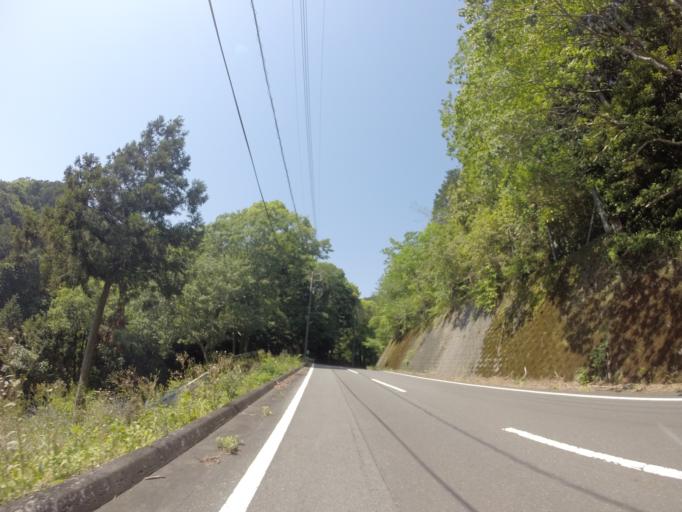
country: JP
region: Shizuoka
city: Fujinomiya
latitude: 35.1486
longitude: 138.5644
